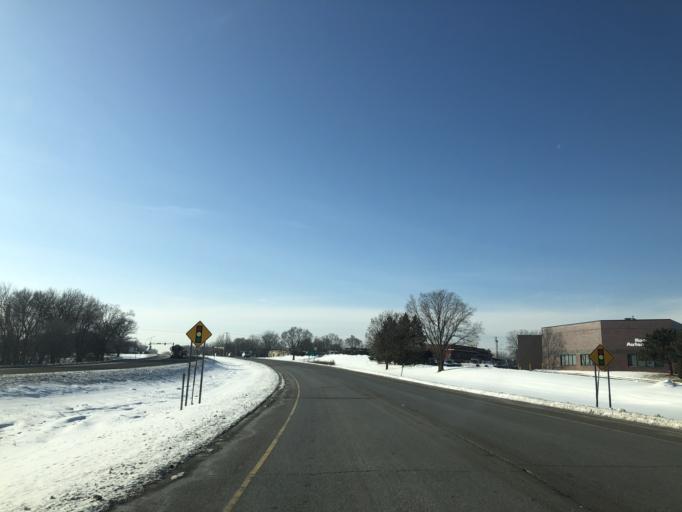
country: US
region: Minnesota
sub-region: Ramsey County
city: New Brighton
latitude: 45.0382
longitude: -93.1946
